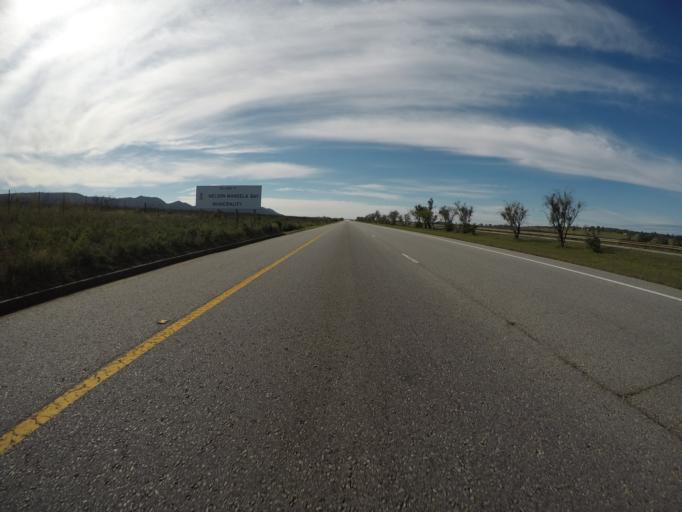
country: ZA
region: Eastern Cape
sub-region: Nelson Mandela Bay Metropolitan Municipality
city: Uitenhage
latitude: -33.9104
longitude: 25.2056
